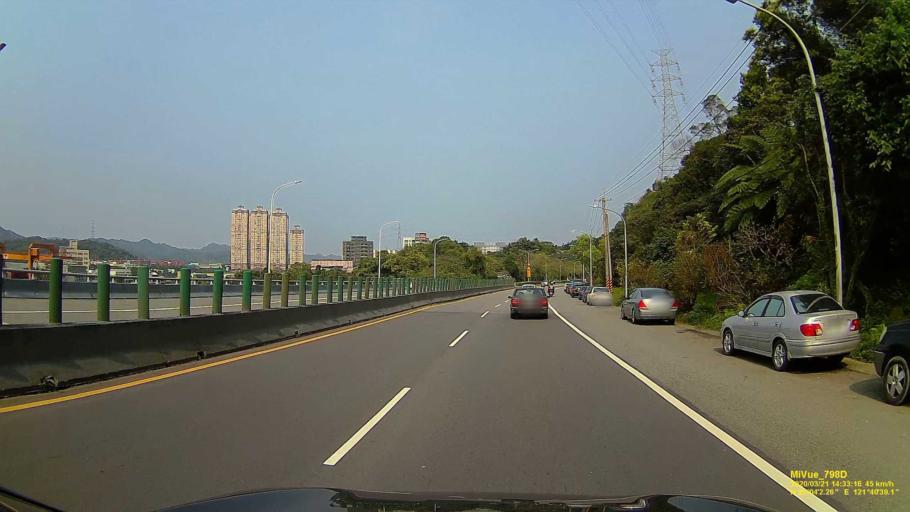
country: TW
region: Taiwan
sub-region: Keelung
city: Keelung
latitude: 25.0674
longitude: 121.6777
